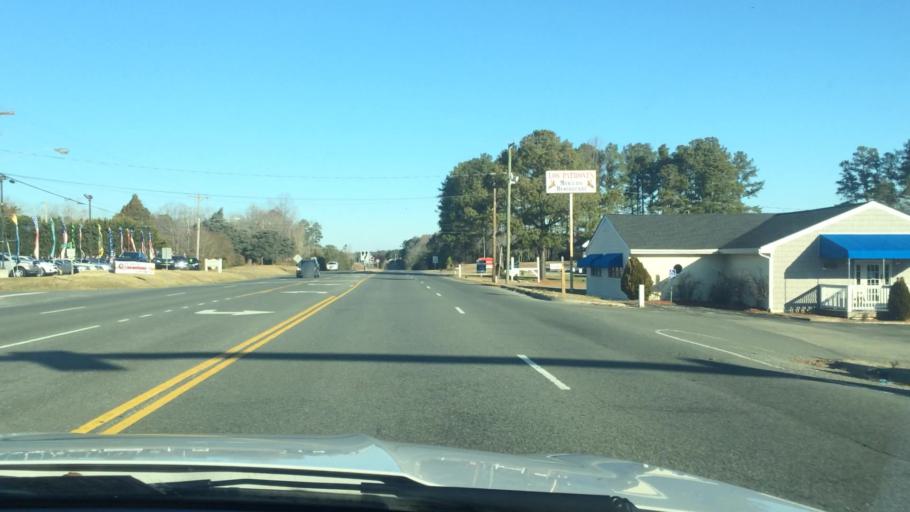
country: US
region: Virginia
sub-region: Lancaster County
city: Kilmarnock
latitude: 37.7272
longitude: -76.3897
